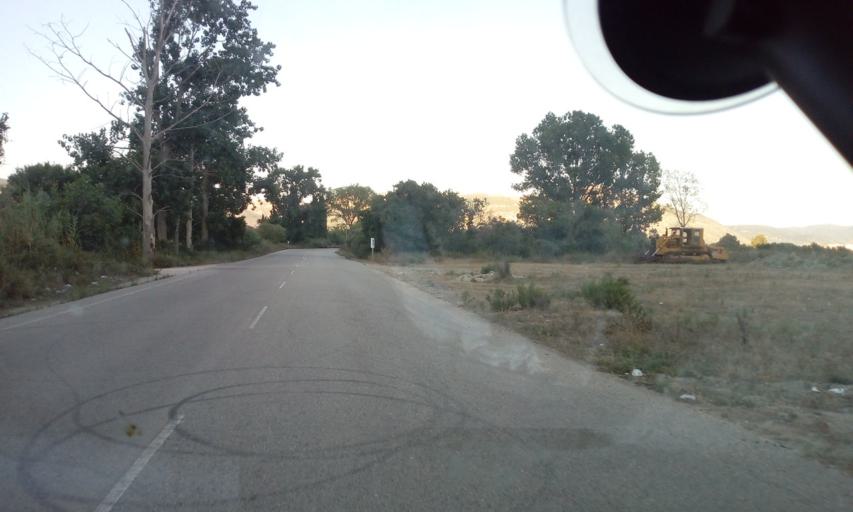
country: GR
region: West Greece
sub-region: Nomos Aitolias kai Akarnanias
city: Kandila
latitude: 38.6783
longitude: 20.9328
